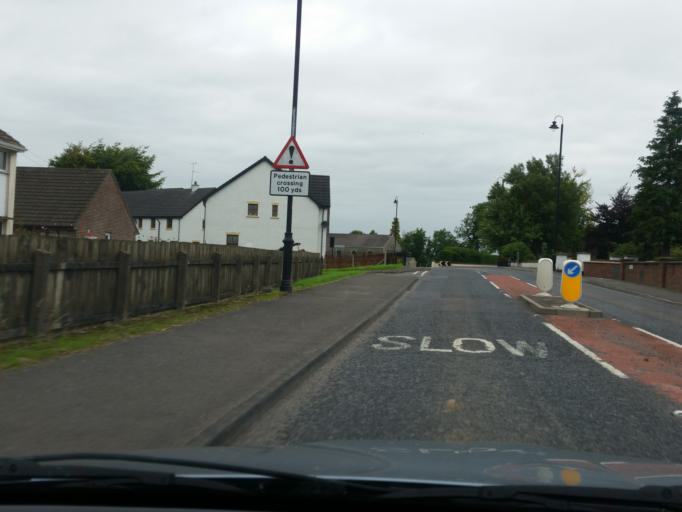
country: GB
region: Northern Ireland
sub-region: Fermanagh District
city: Enniskillen
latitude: 54.2951
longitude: -7.6380
